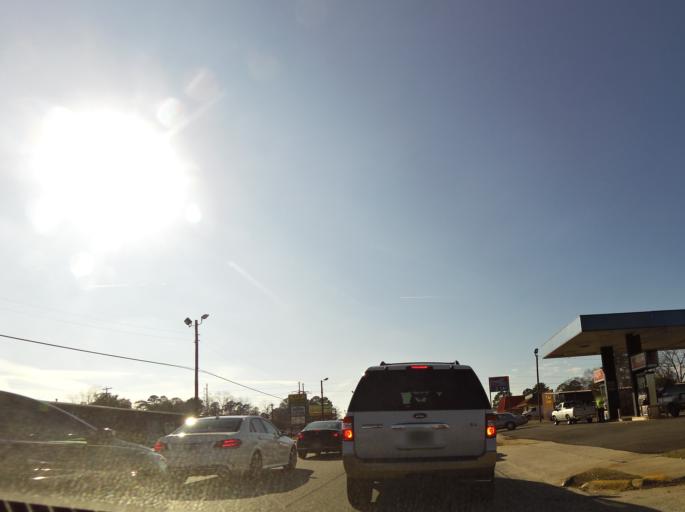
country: US
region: Georgia
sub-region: Houston County
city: Warner Robins
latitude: 32.6183
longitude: -83.6197
